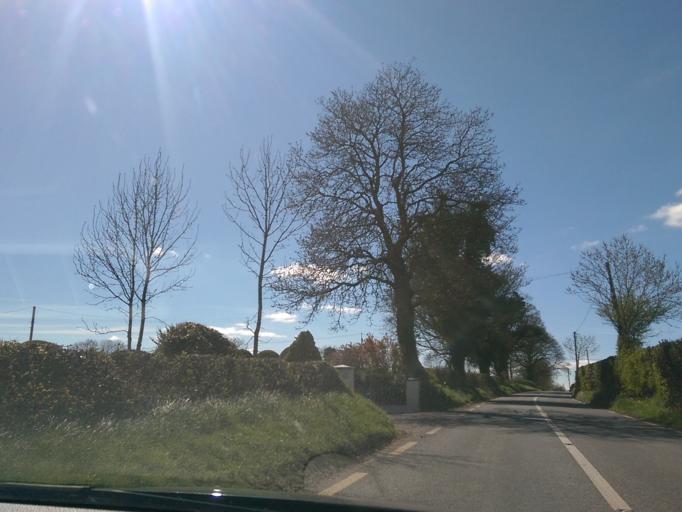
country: IE
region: Leinster
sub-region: Kildare
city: Moone
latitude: 52.9786
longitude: -6.7765
